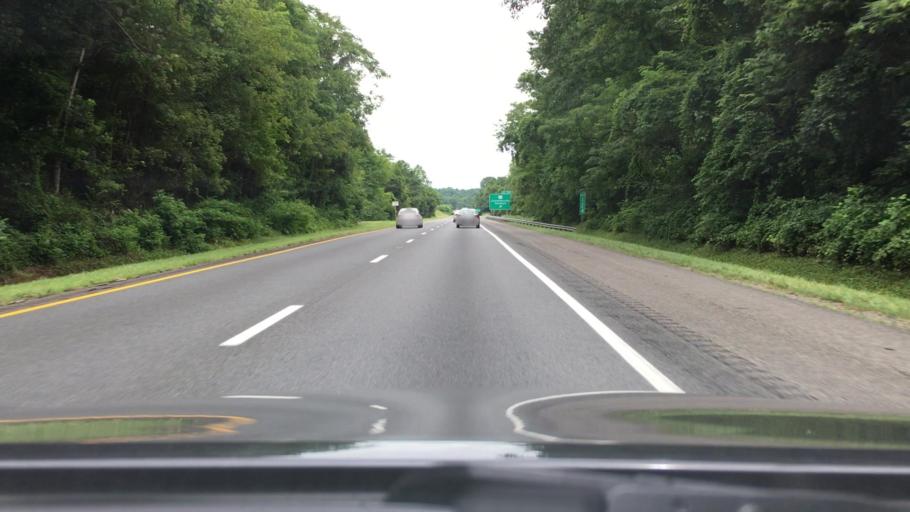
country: US
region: Virginia
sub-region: City of Charlottesville
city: Charlottesville
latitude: 38.0185
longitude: -78.4390
